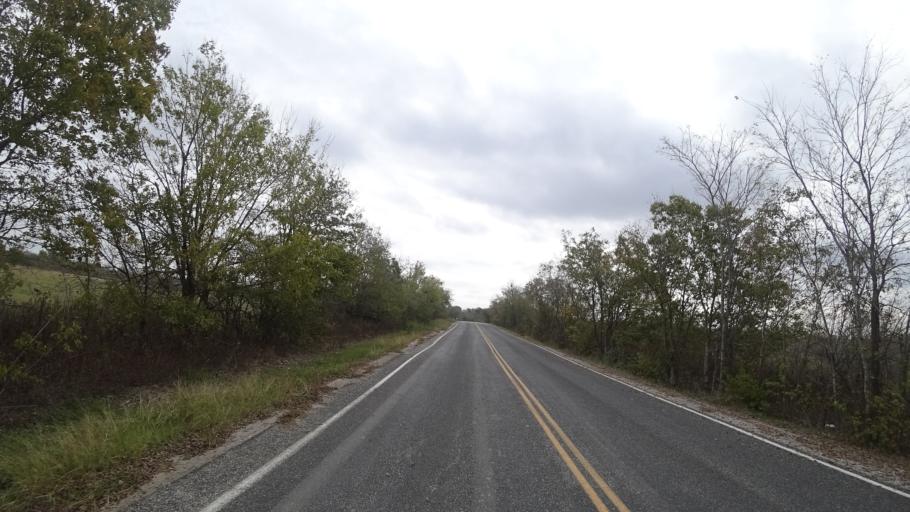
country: US
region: Texas
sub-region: Travis County
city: Pflugerville
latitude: 30.3946
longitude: -97.5886
